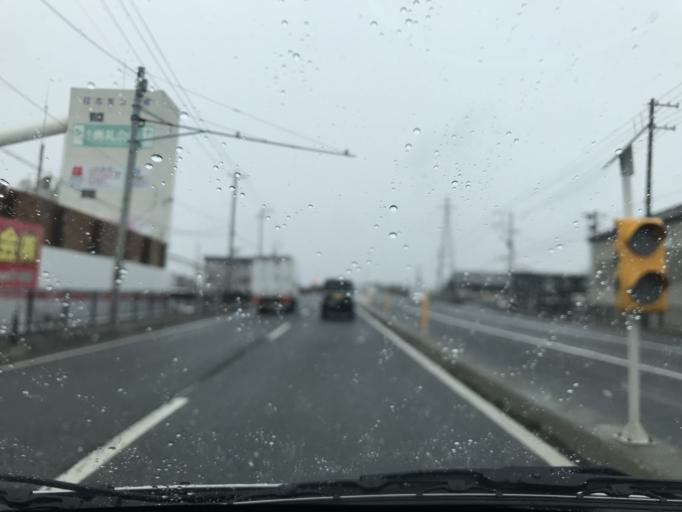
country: JP
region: Iwate
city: Kitakami
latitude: 39.2760
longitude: 141.1014
